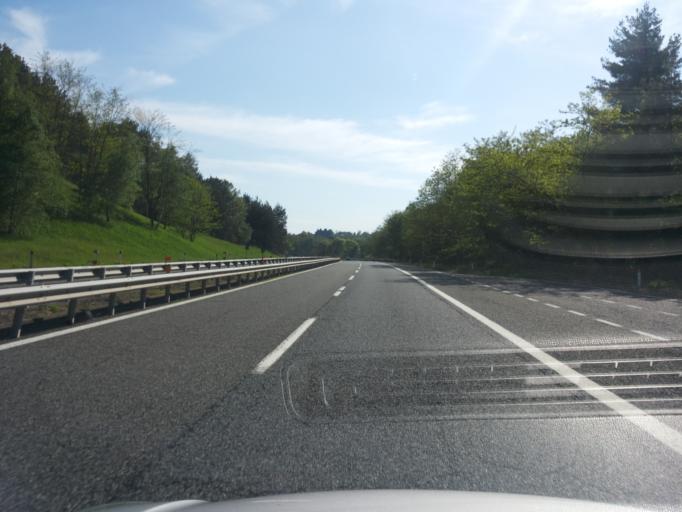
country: IT
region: Piedmont
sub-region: Provincia di Novara
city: Comignago
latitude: 45.7048
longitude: 8.5467
